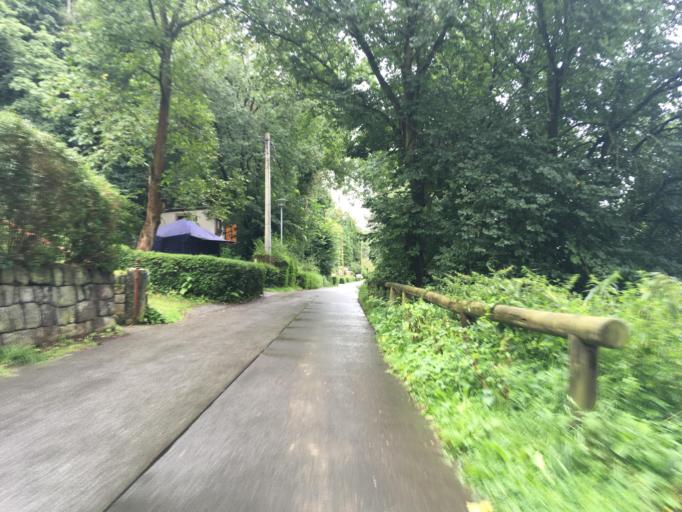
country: DE
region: Saxony
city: Pirna
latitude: 50.9603
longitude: 13.9742
